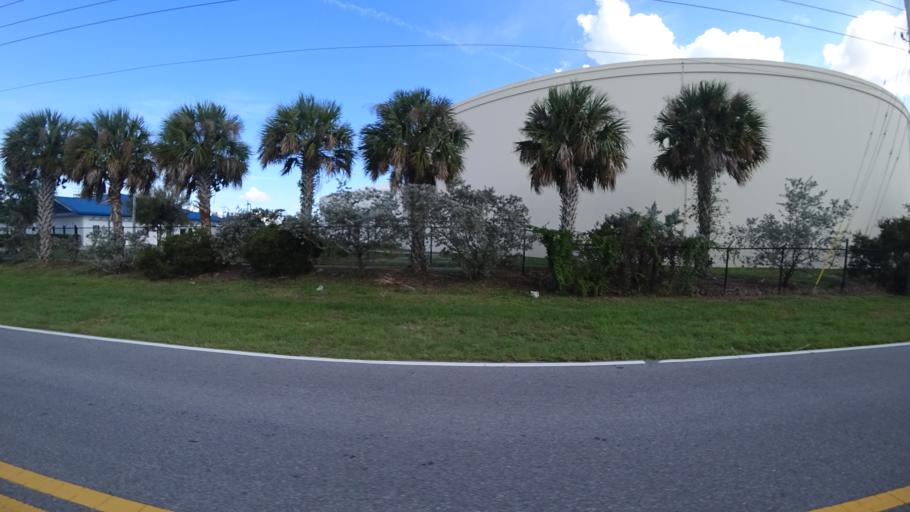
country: US
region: Florida
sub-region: Manatee County
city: South Bradenton
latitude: 27.4563
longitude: -82.6272
